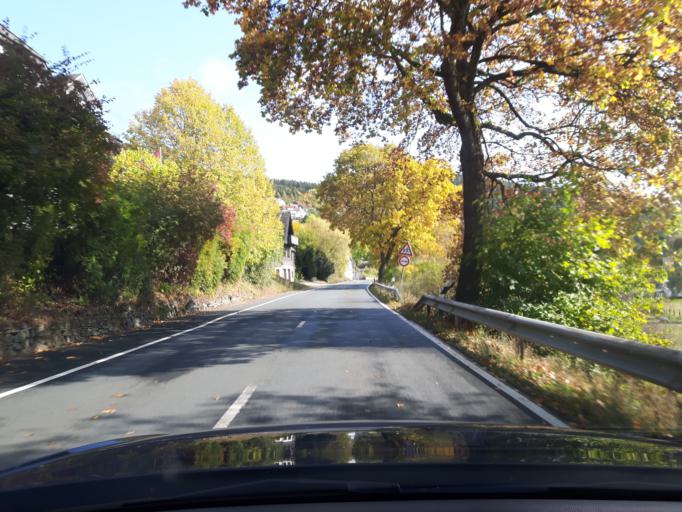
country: DE
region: Hesse
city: Hatzfeld
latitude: 51.0240
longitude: 8.4710
